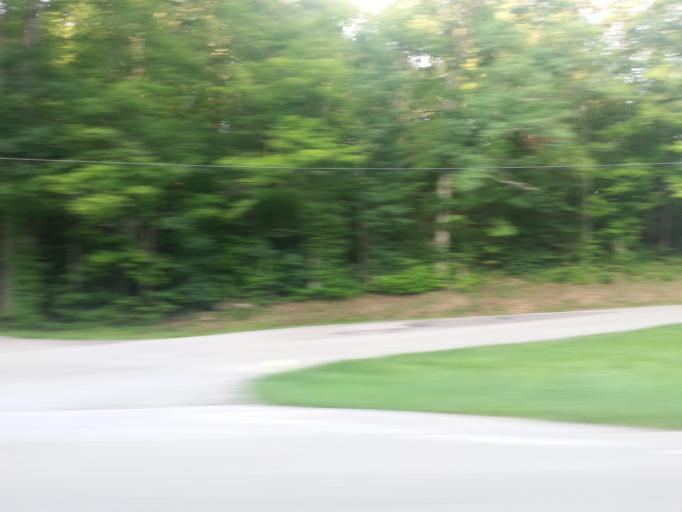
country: US
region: Tennessee
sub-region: Anderson County
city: Norris
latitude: 36.1554
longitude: -84.0305
